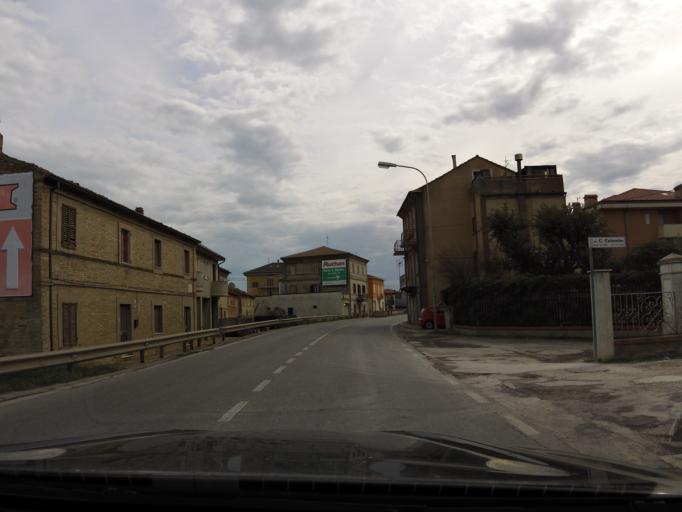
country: IT
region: The Marches
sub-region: Provincia di Macerata
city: Civitanova Marche
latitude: 43.3316
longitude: 13.7122
